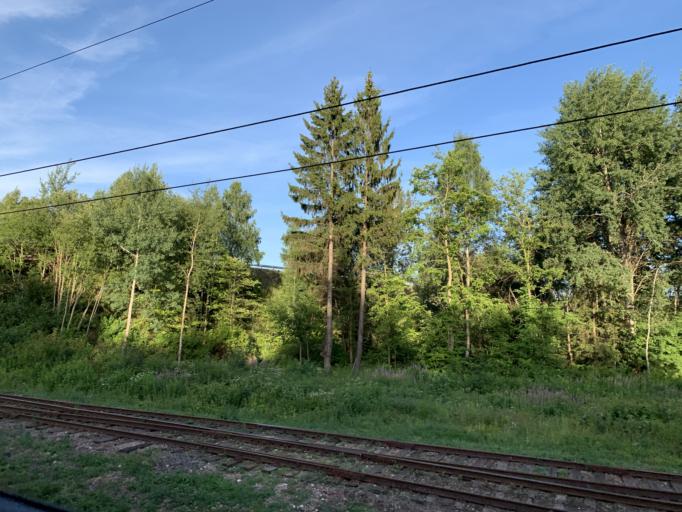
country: BY
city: Fanipol
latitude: 53.7555
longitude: 27.3588
